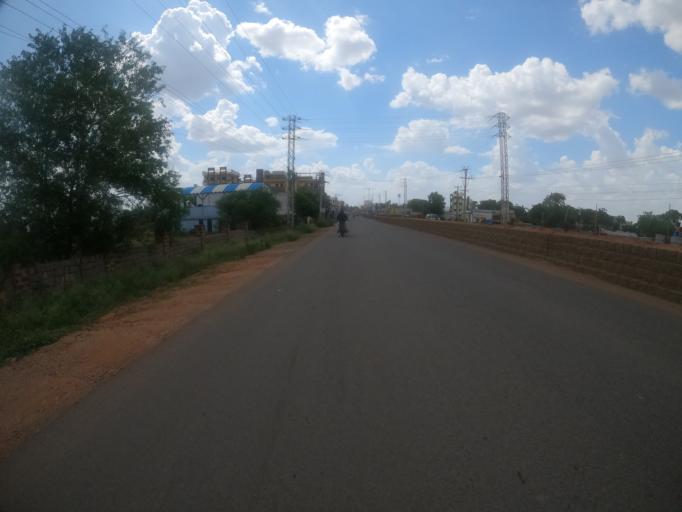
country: IN
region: Telangana
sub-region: Rangareddi
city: Sriramnagar
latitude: 17.3074
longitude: 78.1439
